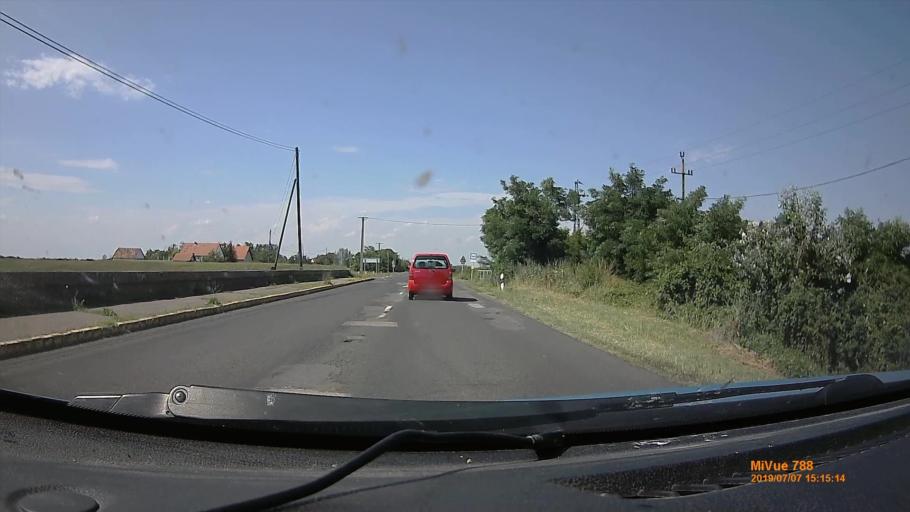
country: HU
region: Jasz-Nagykun-Szolnok
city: Ujszasz
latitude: 47.3160
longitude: 20.0932
